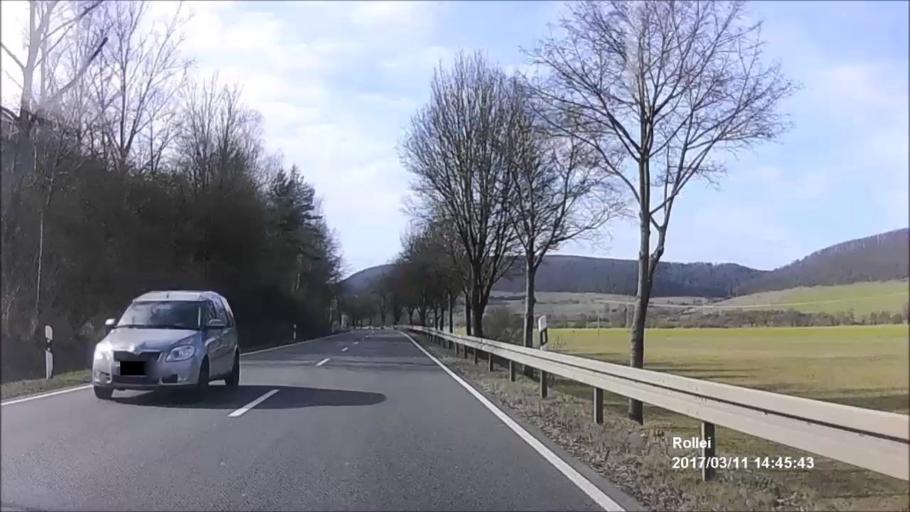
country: DE
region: Thuringia
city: Vachdorf
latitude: 50.5248
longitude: 10.5194
